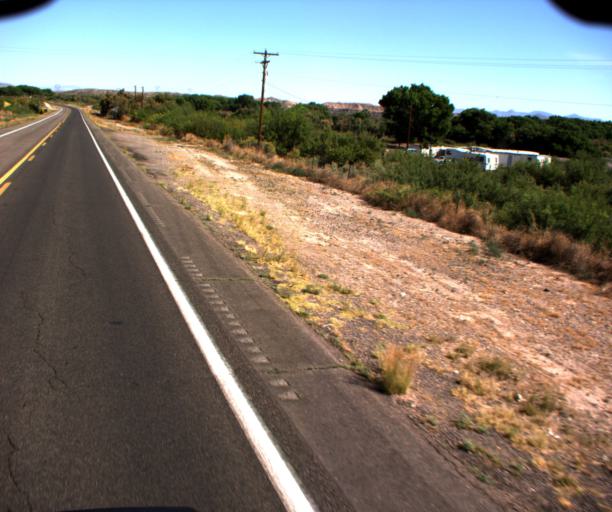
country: US
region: Arizona
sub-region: Greenlee County
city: Clifton
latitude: 32.7369
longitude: -109.1243
